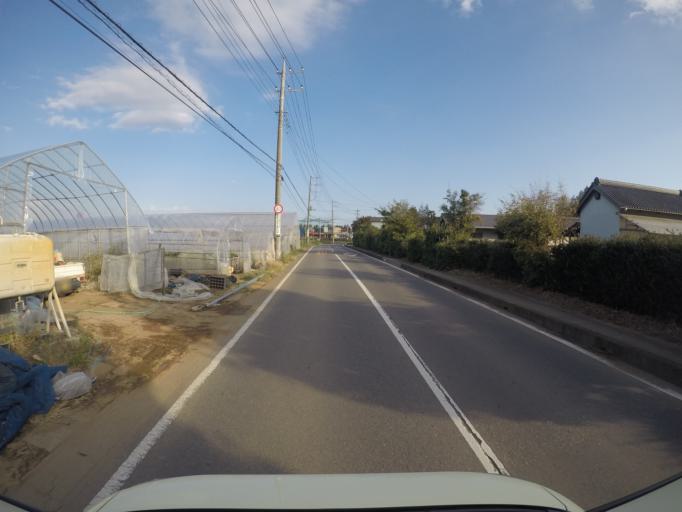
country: JP
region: Ibaraki
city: Naka
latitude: 36.0591
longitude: 140.0985
